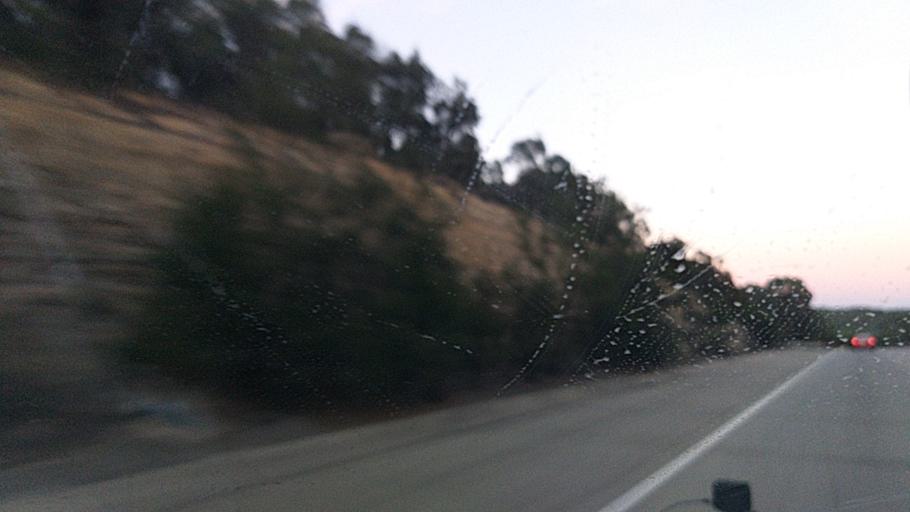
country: AU
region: New South Wales
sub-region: Wingecarribee
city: Bundanoon
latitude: -34.6797
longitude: 150.0564
